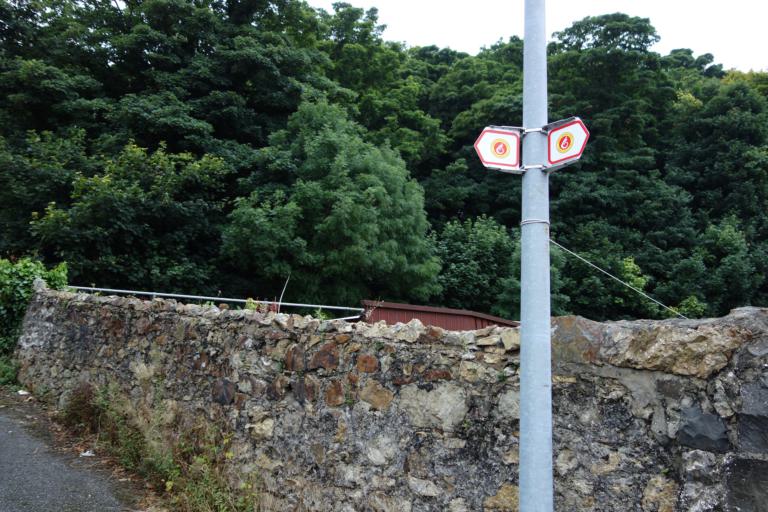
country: GB
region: Wales
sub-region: Conwy
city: Conwy
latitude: 53.2846
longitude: -3.8384
